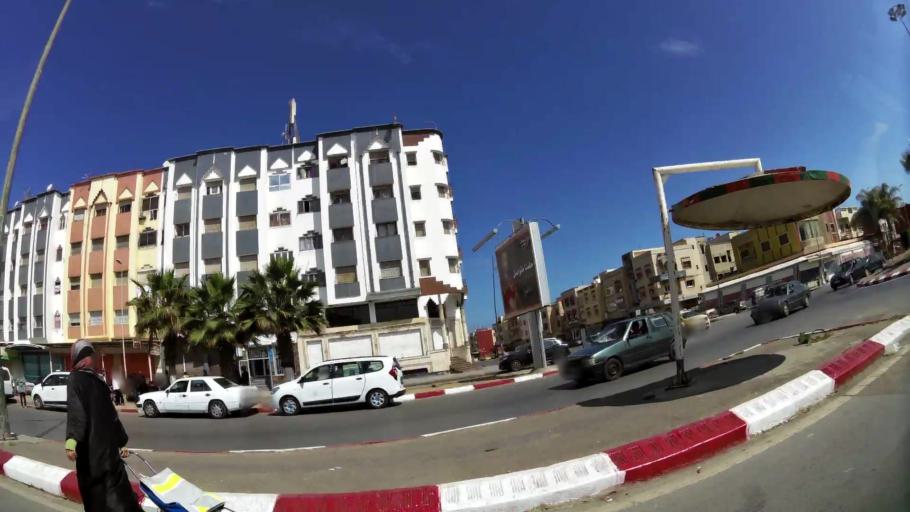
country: MA
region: Rabat-Sale-Zemmour-Zaer
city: Sale
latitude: 34.0686
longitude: -6.7916
